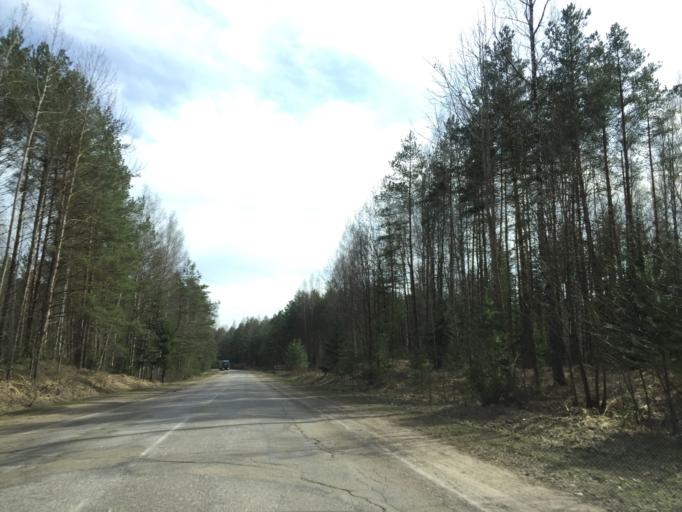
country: LV
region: Ogre
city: Ogre
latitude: 56.8388
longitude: 24.5770
